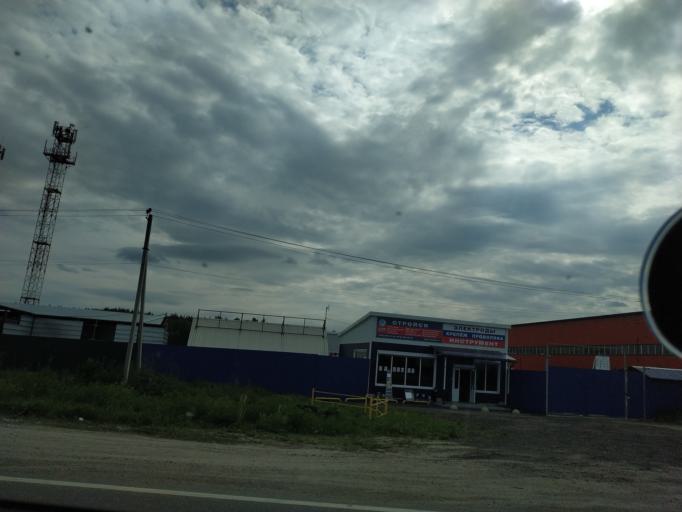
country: RU
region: Moskovskaya
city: Malyshevo
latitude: 55.4831
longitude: 38.3424
